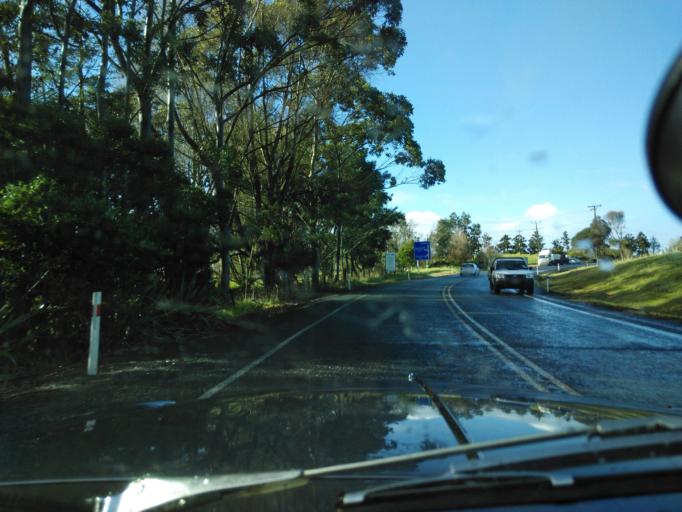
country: NZ
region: Auckland
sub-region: Auckland
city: Rothesay Bay
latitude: -36.6326
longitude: 174.6123
